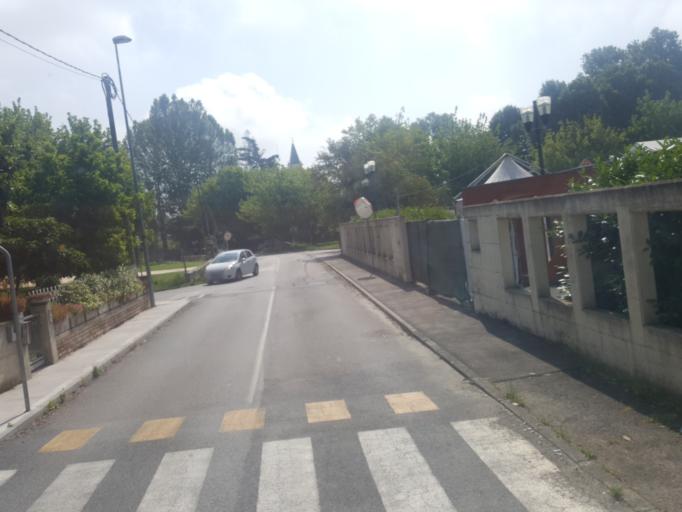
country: IT
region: Veneto
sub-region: Provincia di Rovigo
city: Canaro
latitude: 44.9357
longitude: 11.6744
